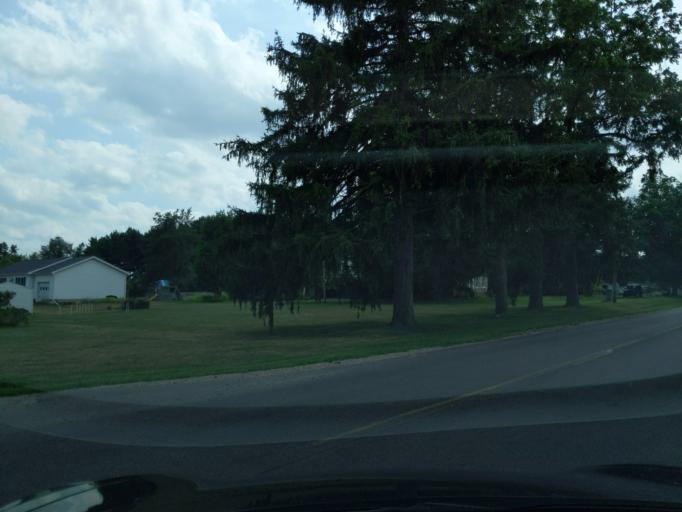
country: US
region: Michigan
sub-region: Eaton County
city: Eaton Rapids
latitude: 42.5095
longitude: -84.6014
